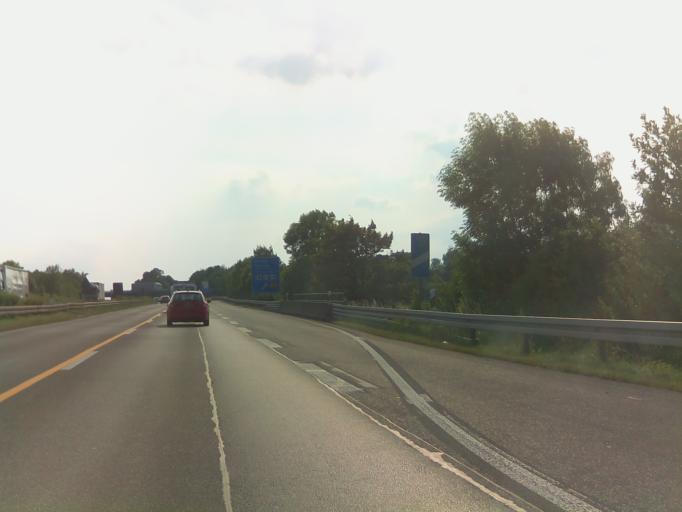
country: DE
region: Hesse
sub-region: Regierungsbezirk Giessen
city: Alsfeld
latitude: 50.7367
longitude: 9.2487
